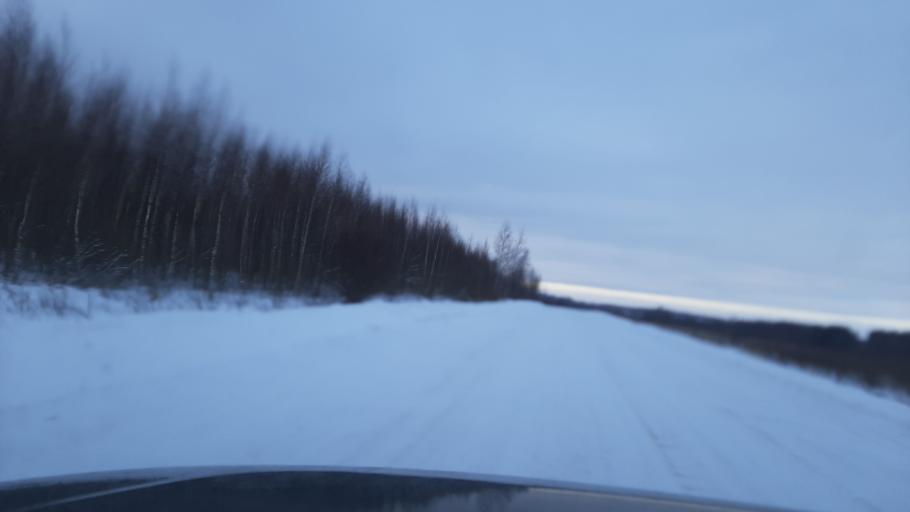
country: RU
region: Kostroma
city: Volgorechensk
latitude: 57.4479
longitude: 41.0022
